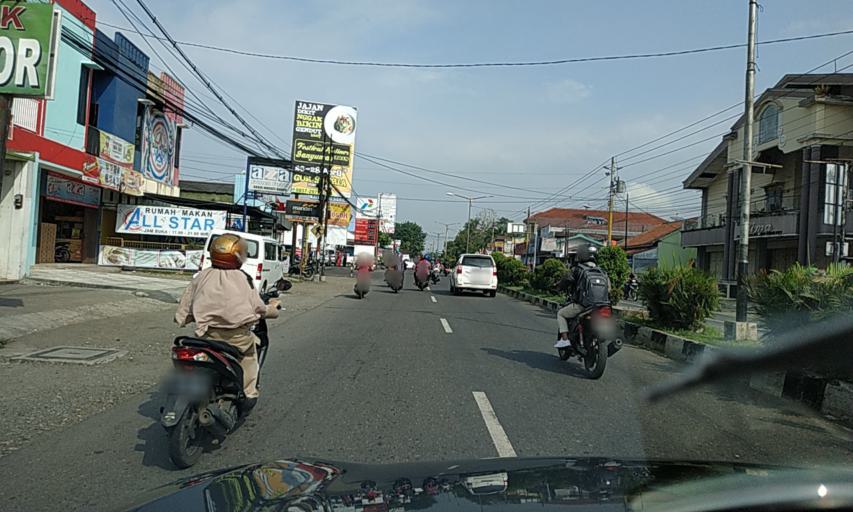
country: ID
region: Central Java
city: Purwokerto
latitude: -7.4223
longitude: 109.2125
